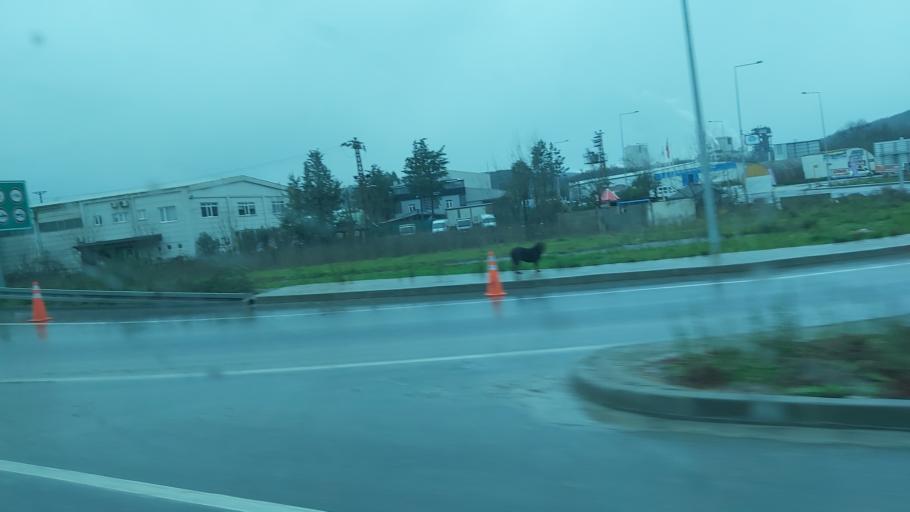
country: TR
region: Istanbul
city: Mahmut Sevket Pasa
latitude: 41.1155
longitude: 29.3029
